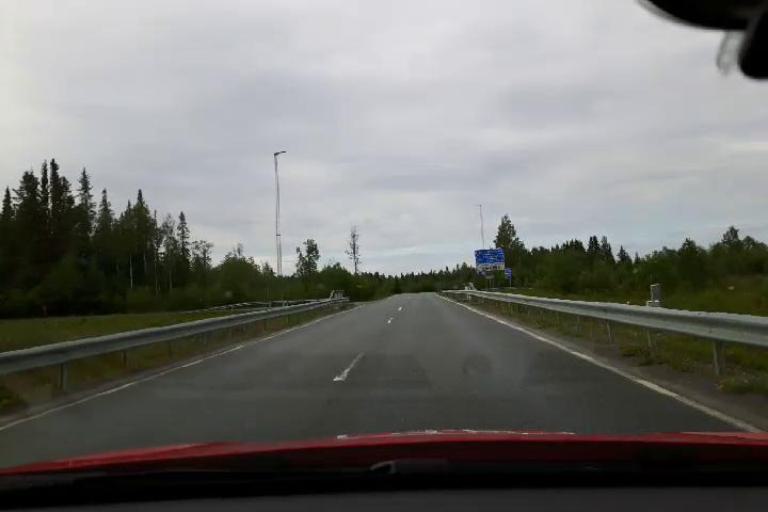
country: SE
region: Jaemtland
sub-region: Bergs Kommun
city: Hoverberg
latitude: 62.9148
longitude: 14.3285
